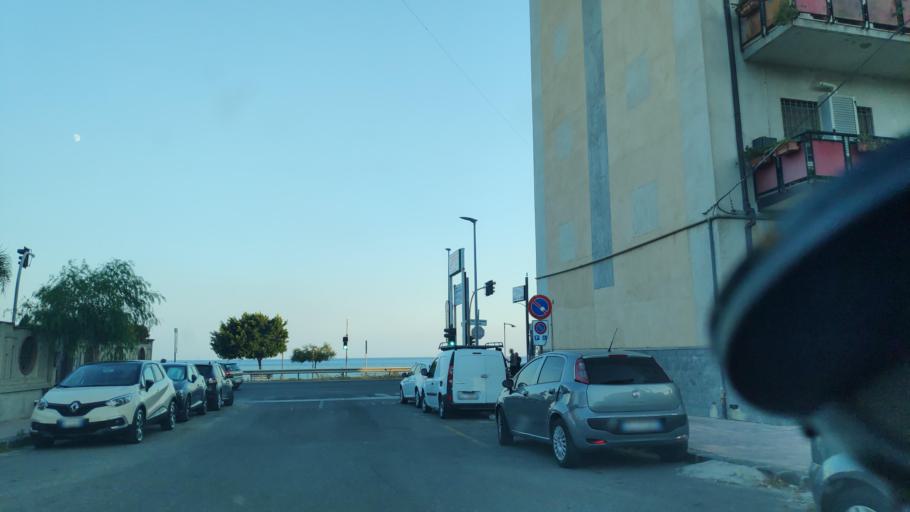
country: IT
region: Calabria
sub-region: Provincia di Reggio Calabria
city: Roccella Ionica
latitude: 38.3186
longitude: 16.3956
